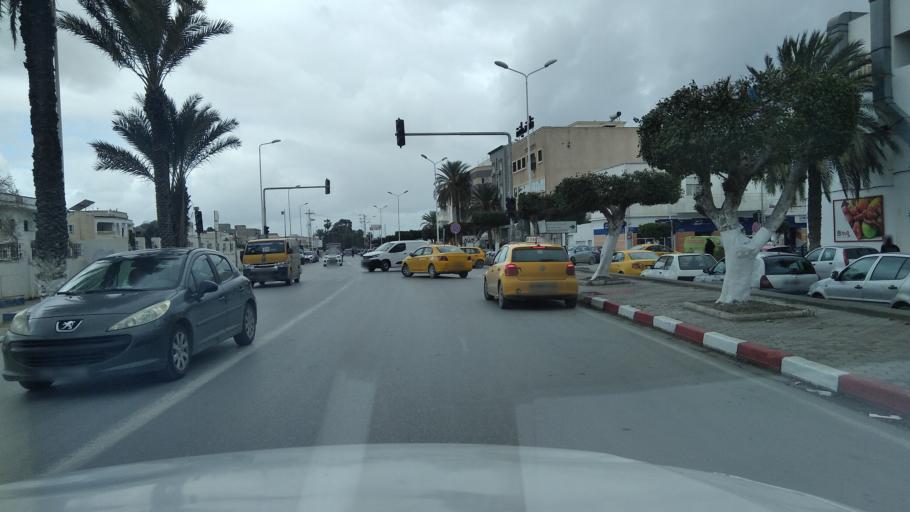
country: TN
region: Bin 'Arus
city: Ben Arous
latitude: 36.7560
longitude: 10.2204
